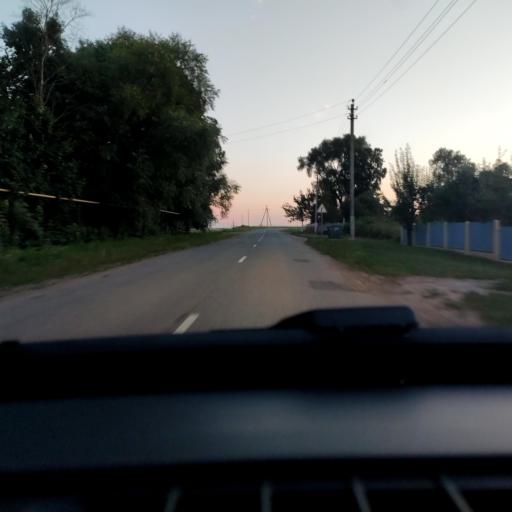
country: RU
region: Lipetsk
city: Zadonsk
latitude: 52.2846
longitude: 38.7435
